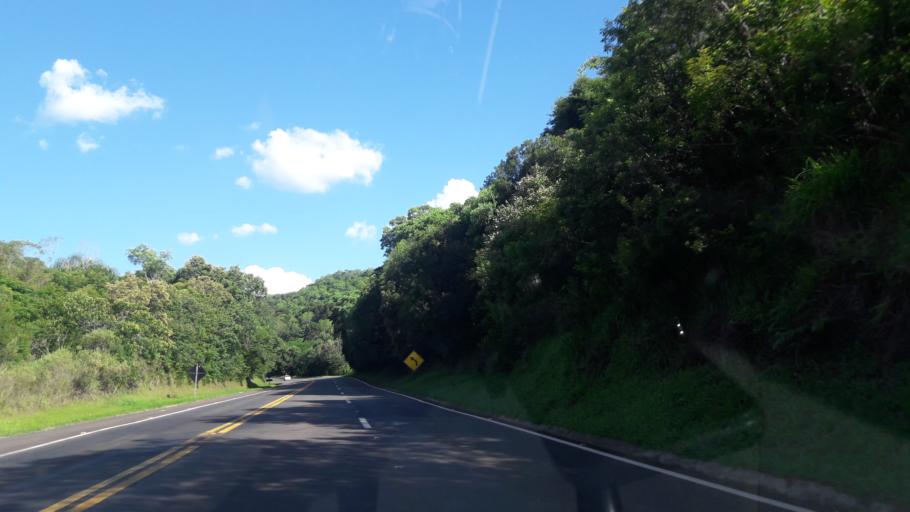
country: BR
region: Parana
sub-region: Laranjeiras Do Sul
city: Laranjeiras do Sul
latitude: -25.4176
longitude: -52.0575
